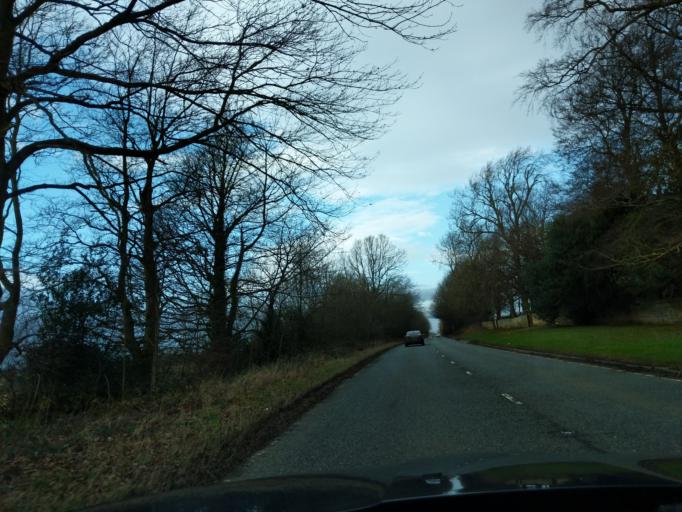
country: GB
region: England
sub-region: Northumberland
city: Darras Hall
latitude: 55.0712
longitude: -1.7930
